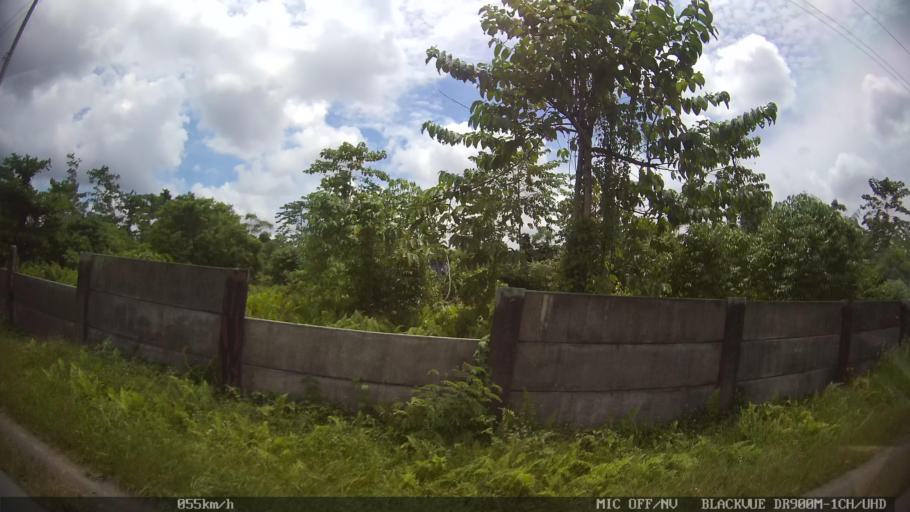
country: ID
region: North Sumatra
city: Medan
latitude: 3.6010
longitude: 98.7286
